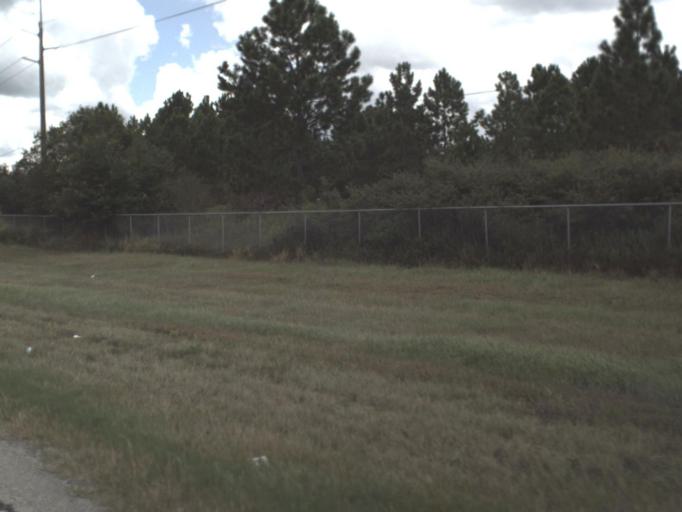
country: US
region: Florida
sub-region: Polk County
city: Mulberry
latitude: 27.8946
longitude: -81.9295
